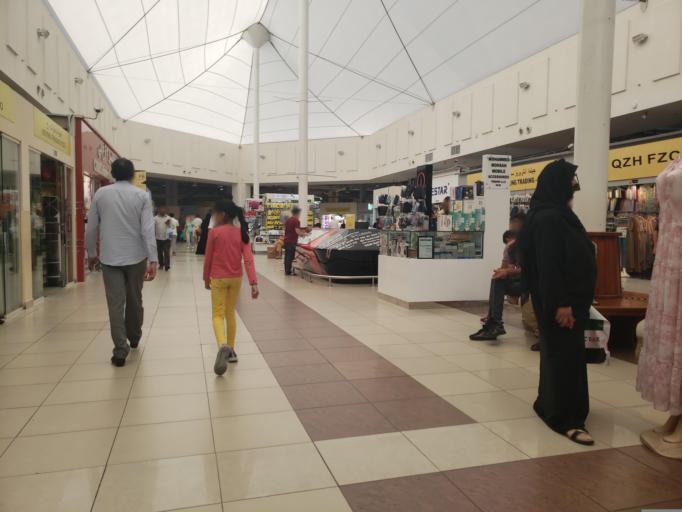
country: AE
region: Ash Shariqah
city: Sharjah
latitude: 25.1743
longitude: 55.4165
